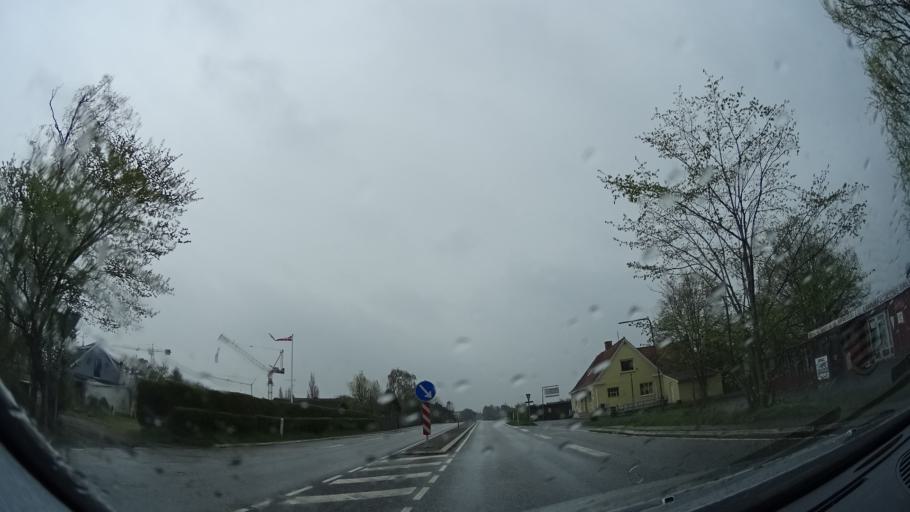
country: DK
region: Zealand
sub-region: Holbaek Kommune
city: Holbaek
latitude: 55.7711
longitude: 11.6277
